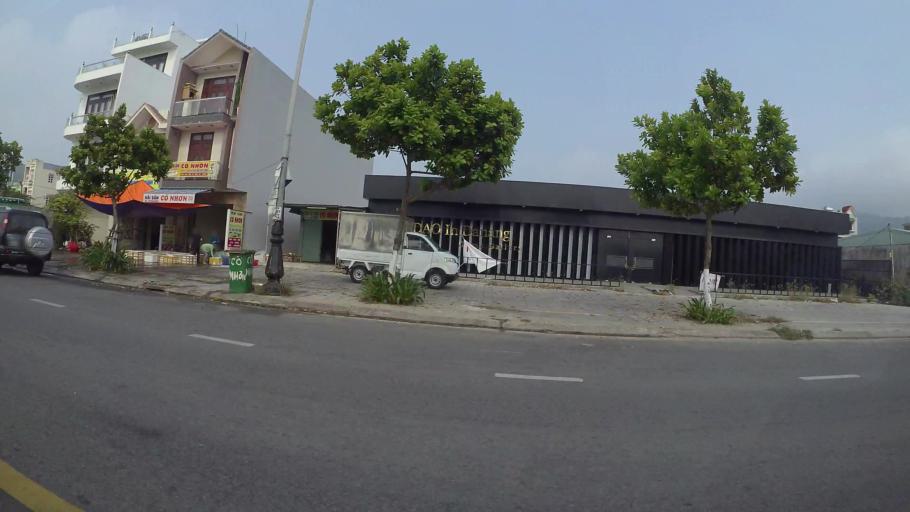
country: VN
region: Da Nang
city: Son Tra
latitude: 16.0979
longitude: 108.2537
